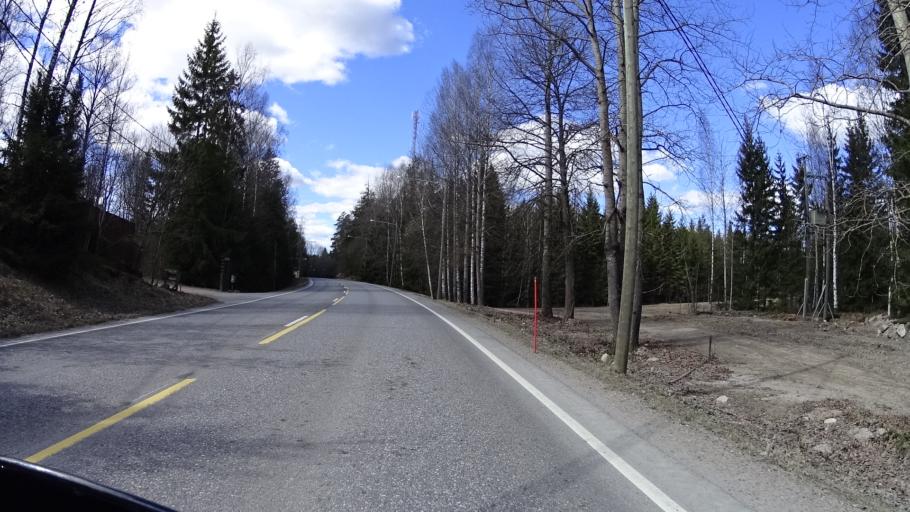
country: FI
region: Uusimaa
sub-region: Helsinki
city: Espoo
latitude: 60.2528
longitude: 24.5191
